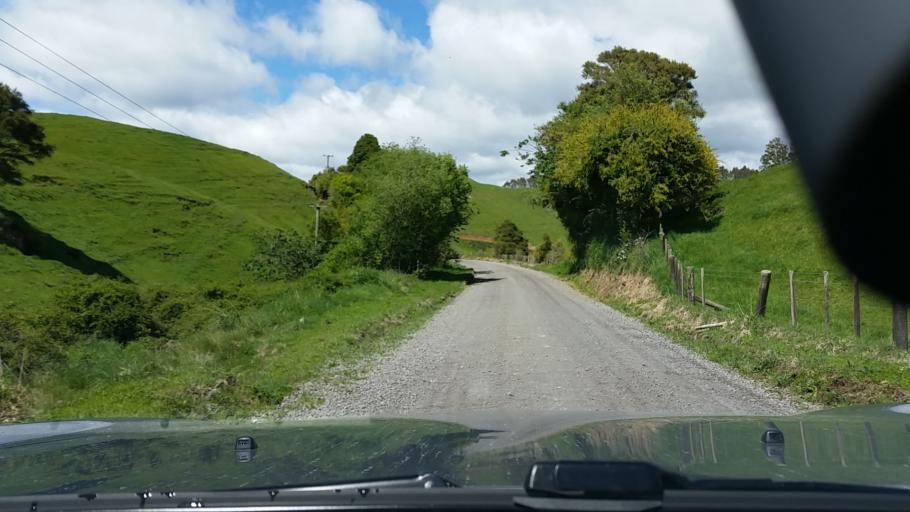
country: NZ
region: Bay of Plenty
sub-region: Rotorua District
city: Rotorua
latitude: -38.3637
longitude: 176.1232
